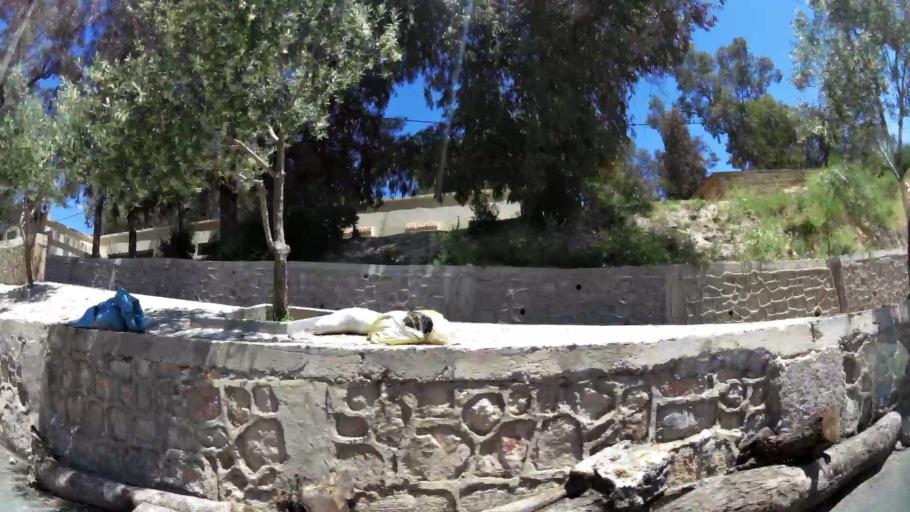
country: MA
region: Meknes-Tafilalet
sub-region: Meknes
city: Meknes
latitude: 33.9072
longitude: -5.5646
